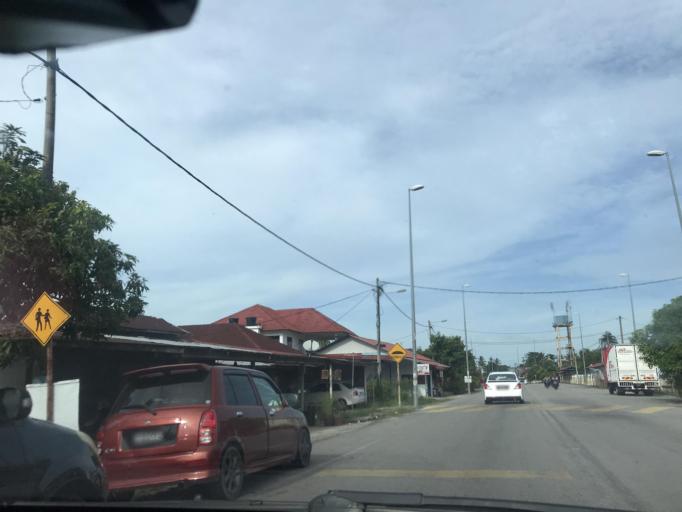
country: MY
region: Kelantan
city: Kota Bharu
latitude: 6.1379
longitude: 102.2137
